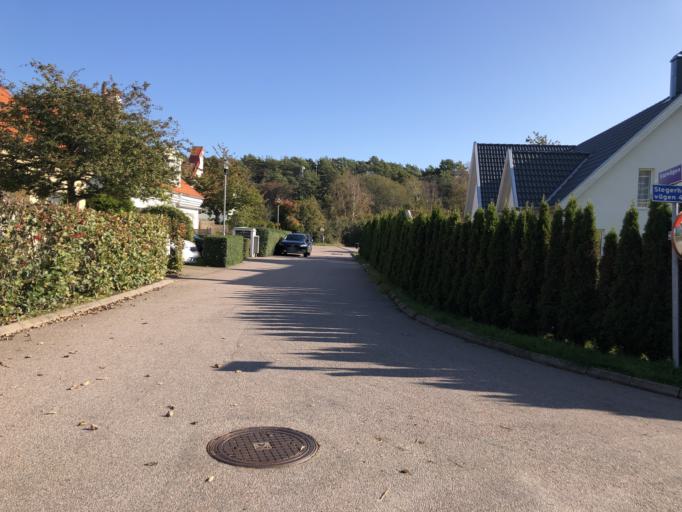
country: SE
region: Vaestra Goetaland
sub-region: Goteborg
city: Billdal
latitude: 57.6186
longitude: 11.8854
